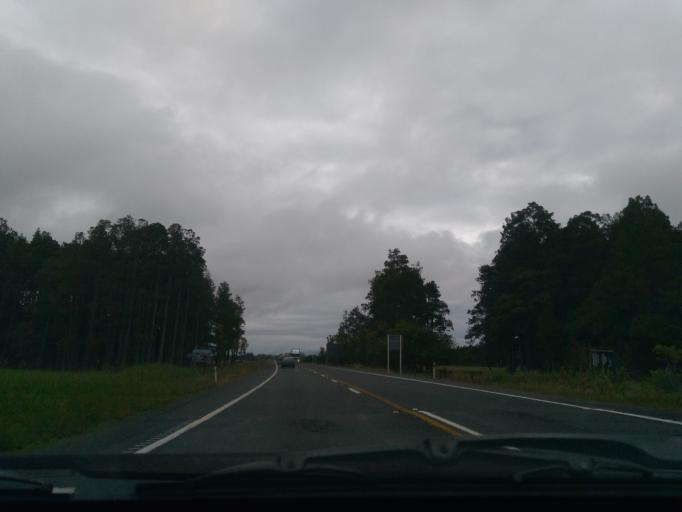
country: NZ
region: Northland
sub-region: Whangarei
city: Ruakaka
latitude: -35.9841
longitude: 174.4308
